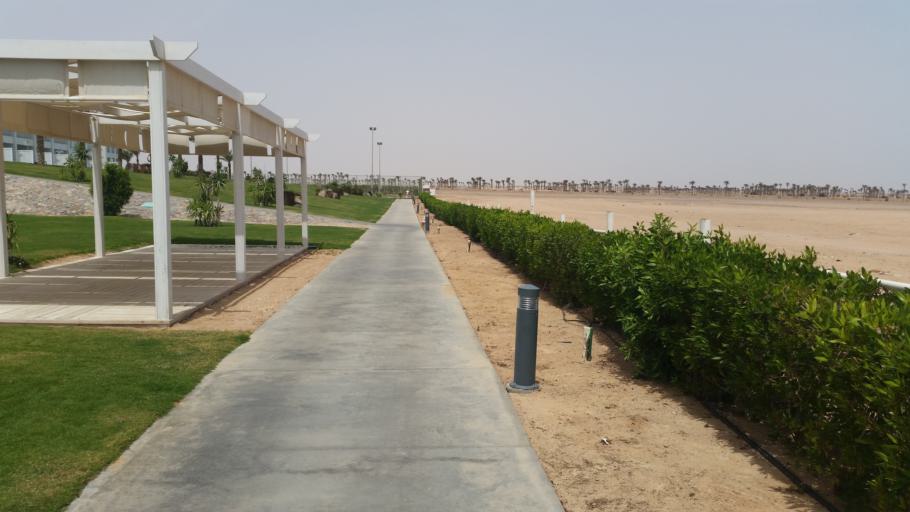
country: EG
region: Red Sea
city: Makadi Bay
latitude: 26.9836
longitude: 33.8753
